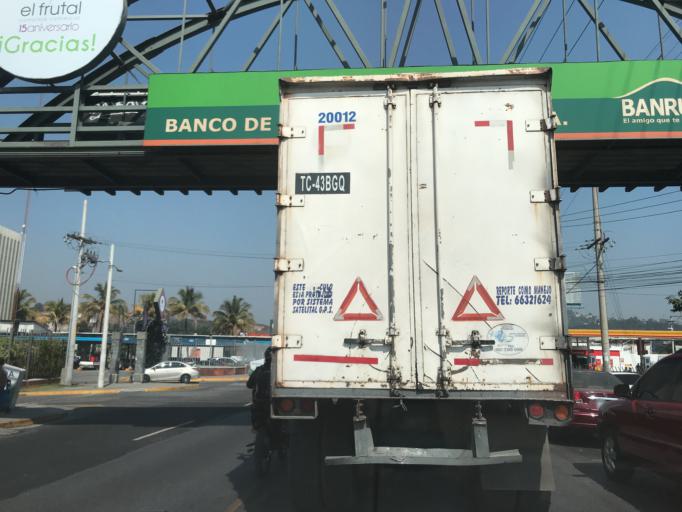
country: GT
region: Guatemala
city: Petapa
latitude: 14.5217
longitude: -90.5636
